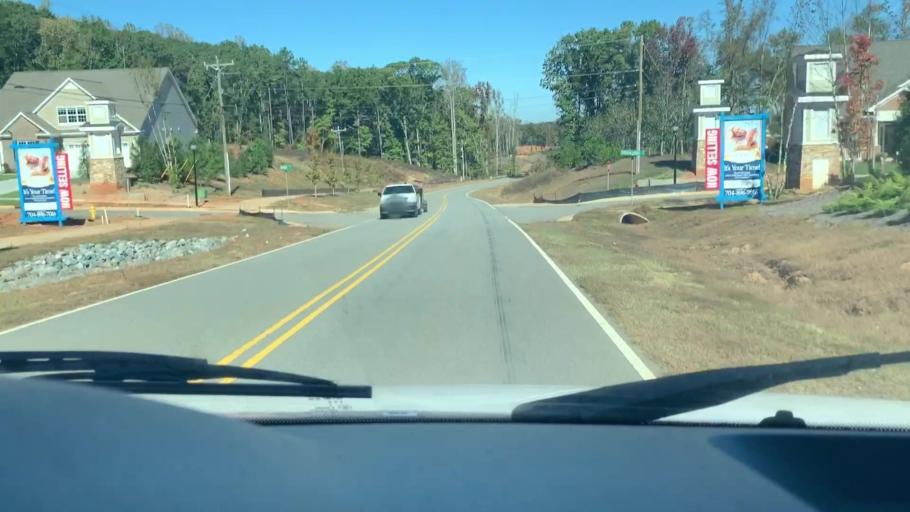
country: US
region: North Carolina
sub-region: Gaston County
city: Davidson
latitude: 35.4618
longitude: -80.8214
